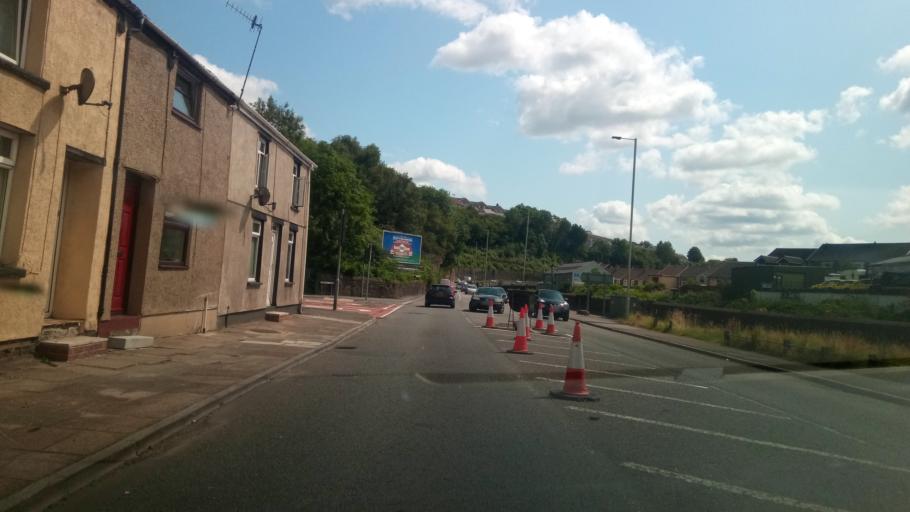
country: GB
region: Wales
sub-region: Rhondda Cynon Taf
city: Pontypridd
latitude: 51.6046
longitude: -3.3522
